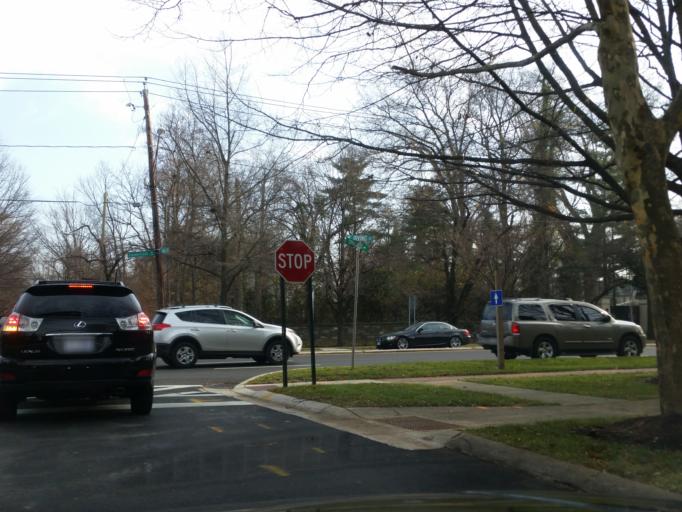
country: US
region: Maryland
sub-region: Montgomery County
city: Chevy Chase Village
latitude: 38.9694
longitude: -77.0774
